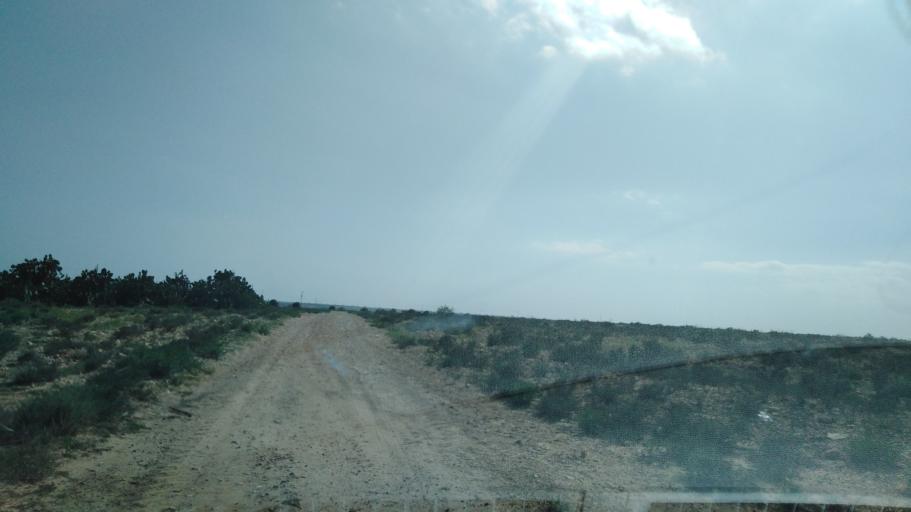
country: TN
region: Safaqis
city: Bi'r `Ali Bin Khalifah
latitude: 34.7984
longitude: 10.3753
